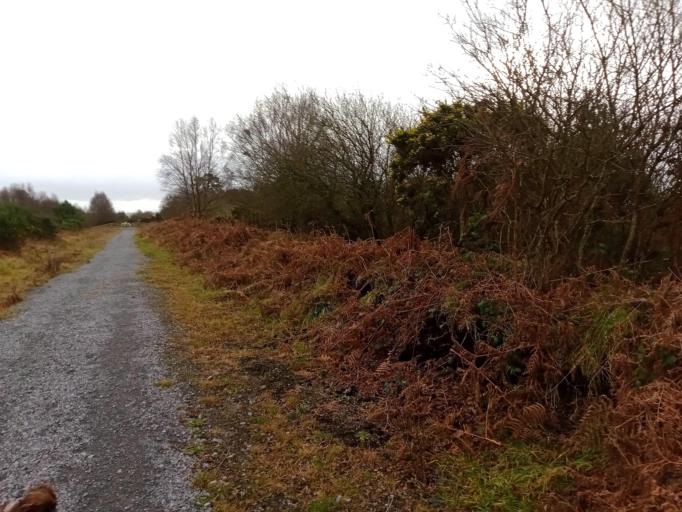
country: IE
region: Munster
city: Thurles
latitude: 52.5944
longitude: -7.7430
